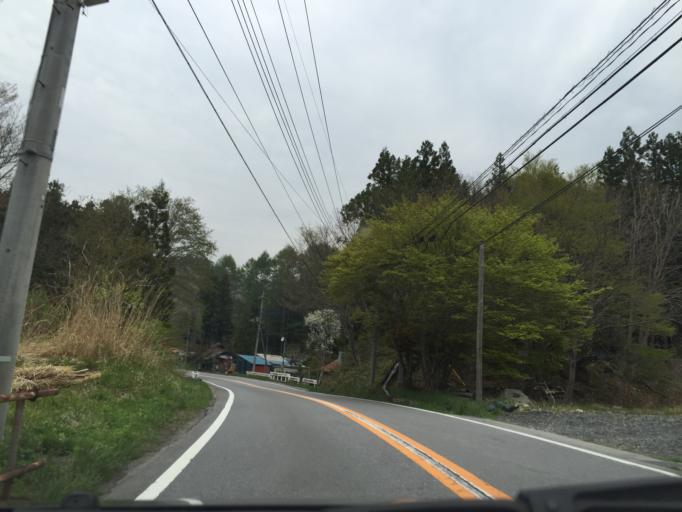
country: JP
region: Tochigi
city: Nikko
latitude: 37.0186
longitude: 139.7305
